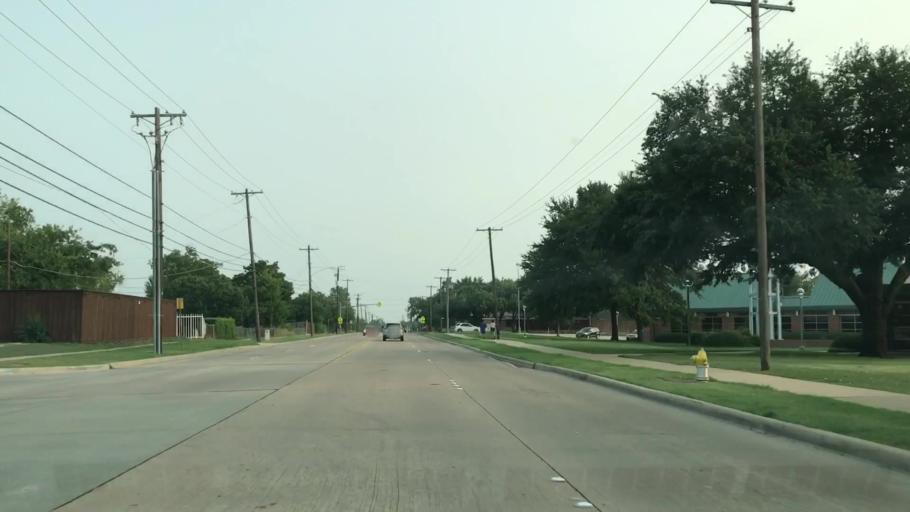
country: US
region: Texas
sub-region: Dallas County
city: Garland
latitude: 32.8985
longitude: -96.6222
